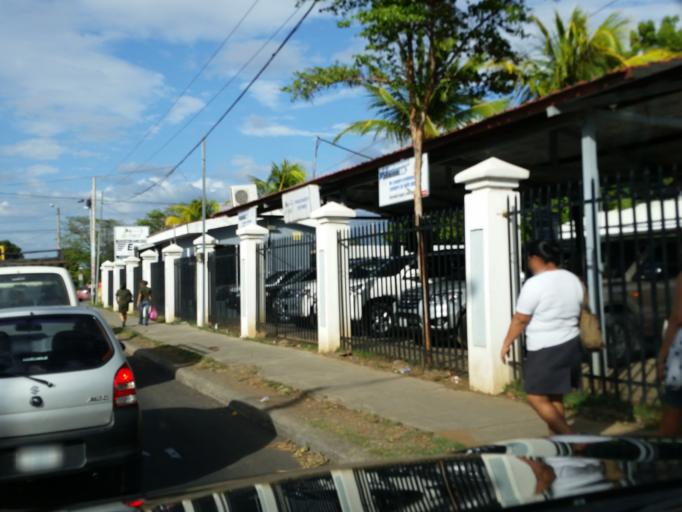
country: NI
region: Managua
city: Managua
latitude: 12.1260
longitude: -86.2563
